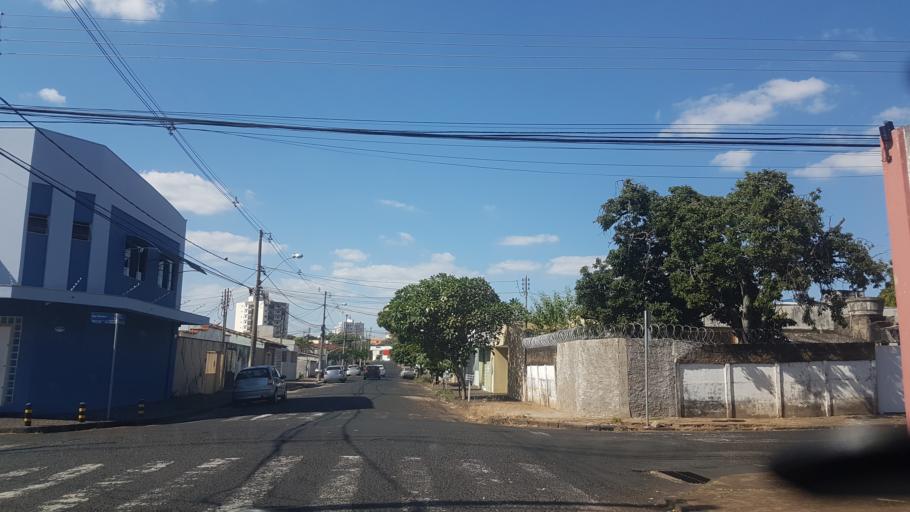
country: BR
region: Minas Gerais
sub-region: Uberlandia
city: Uberlandia
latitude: -18.9059
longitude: -48.2763
